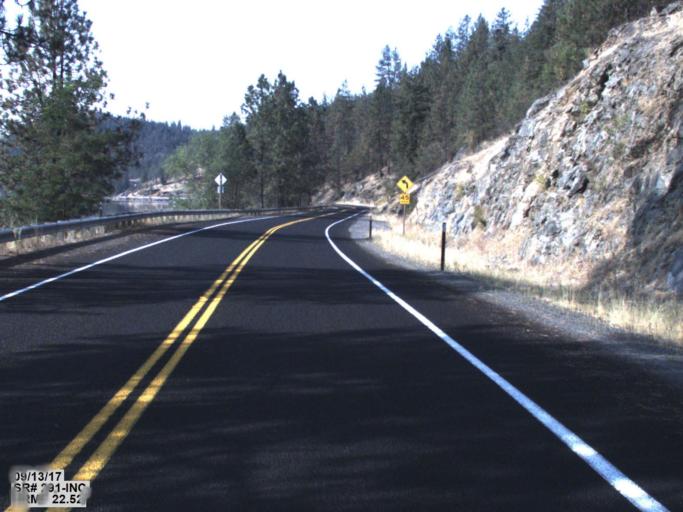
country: US
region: Washington
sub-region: Spokane County
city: Deer Park
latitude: 47.8889
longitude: -117.6895
